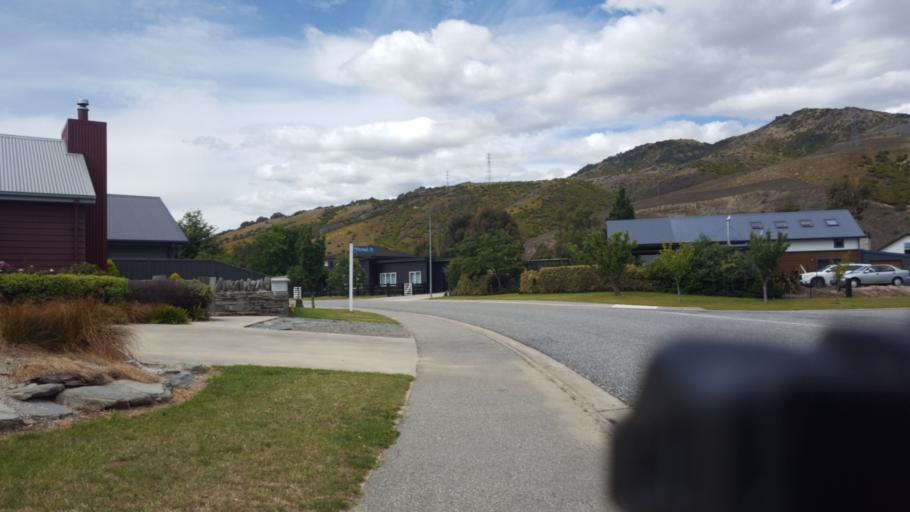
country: NZ
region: Otago
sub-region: Queenstown-Lakes District
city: Wanaka
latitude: -45.0402
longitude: 169.2173
